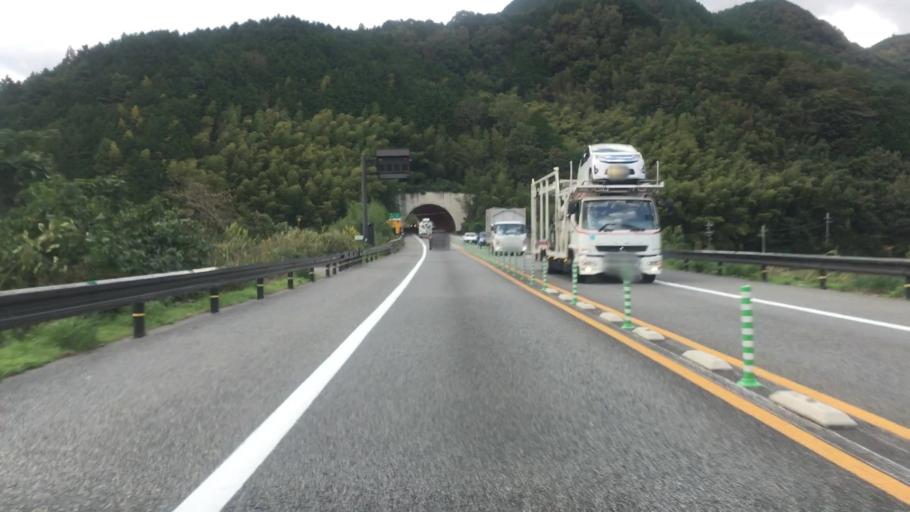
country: JP
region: Kyoto
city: Fukuchiyama
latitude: 35.2712
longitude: 134.9961
